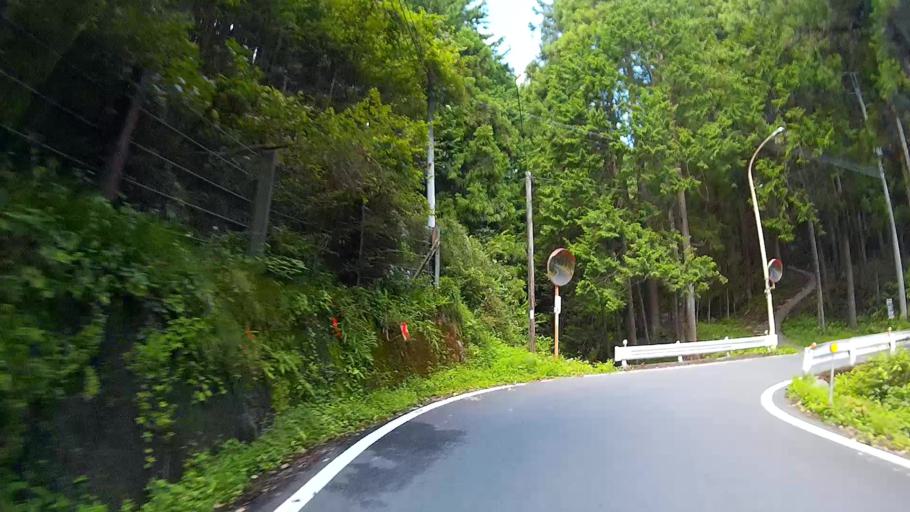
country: JP
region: Saitama
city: Chichibu
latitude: 35.9240
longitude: 139.1513
